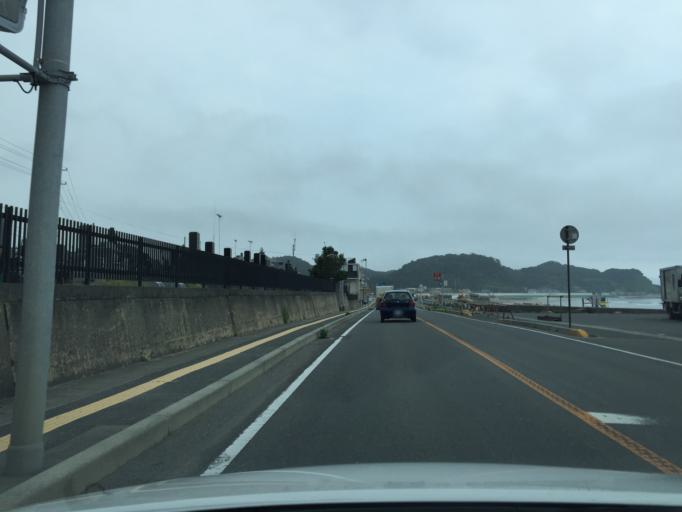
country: JP
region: Fukushima
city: Iwaki
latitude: 36.9519
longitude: 140.9357
